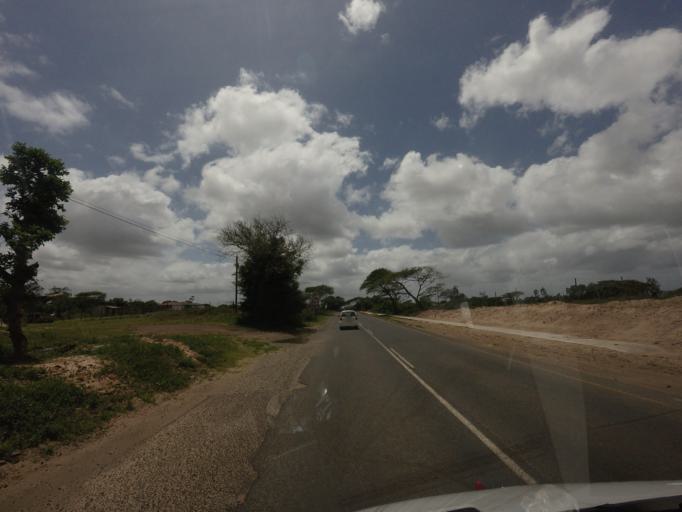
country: ZA
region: KwaZulu-Natal
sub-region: uMkhanyakude District Municipality
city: Mtubatuba
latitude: -28.3787
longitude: 32.3673
